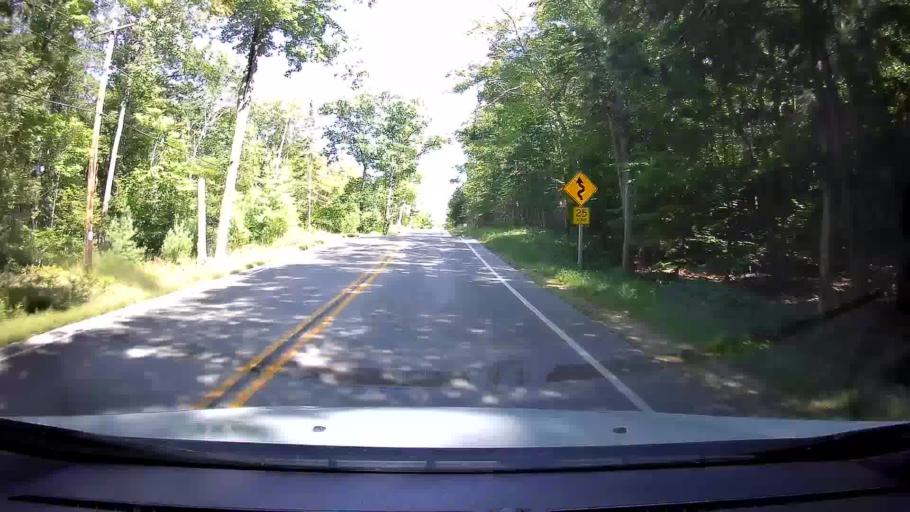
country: US
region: Michigan
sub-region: Delta County
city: Escanaba
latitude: 45.2892
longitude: -86.9964
